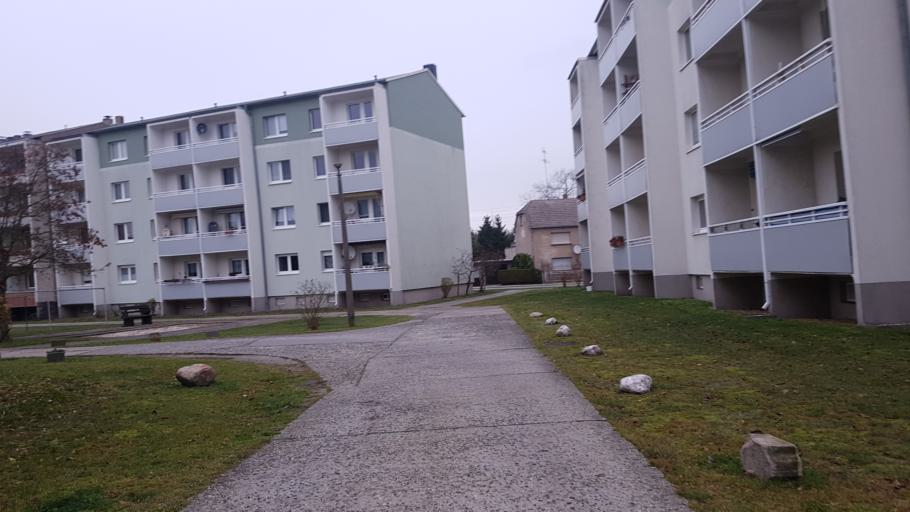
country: DE
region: Brandenburg
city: Ruckersdorf
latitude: 51.5682
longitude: 13.5716
